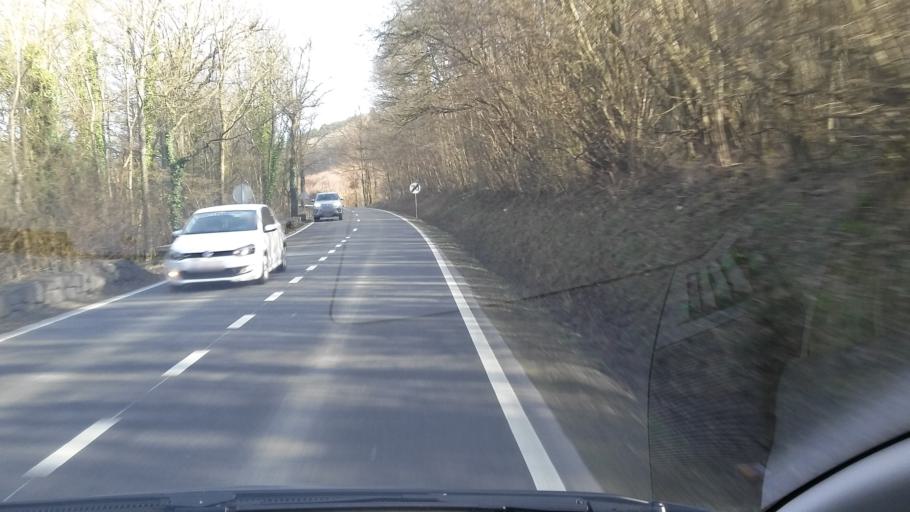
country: BE
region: Wallonia
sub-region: Province du Luxembourg
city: Durbuy
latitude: 50.3582
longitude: 5.5092
